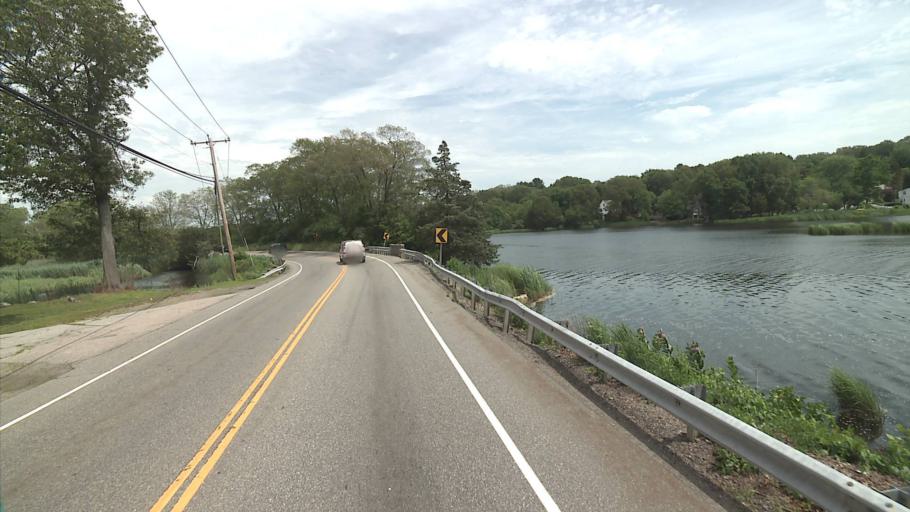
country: US
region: Connecticut
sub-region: New London County
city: Norwich
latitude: 41.4854
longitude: -72.0530
